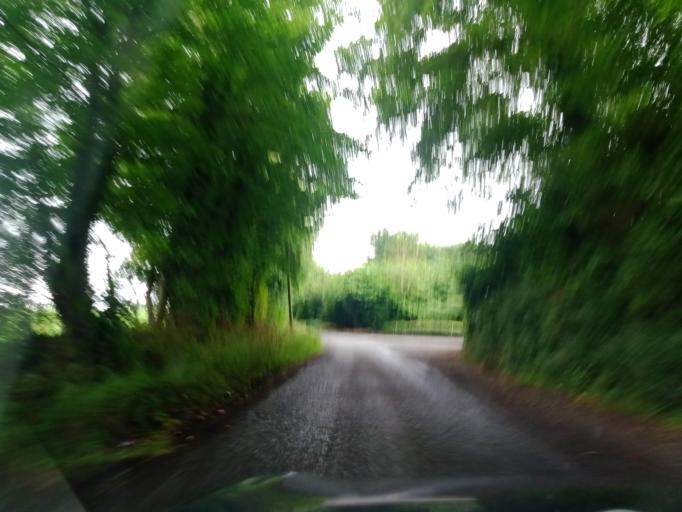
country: IE
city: Ballylinan
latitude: 52.9211
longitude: -7.0758
